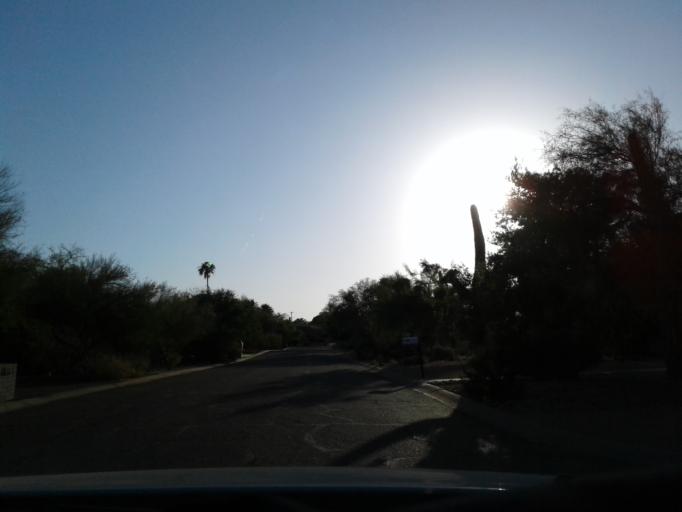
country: US
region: Arizona
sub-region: Maricopa County
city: Paradise Valley
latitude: 33.5212
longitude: -111.9922
